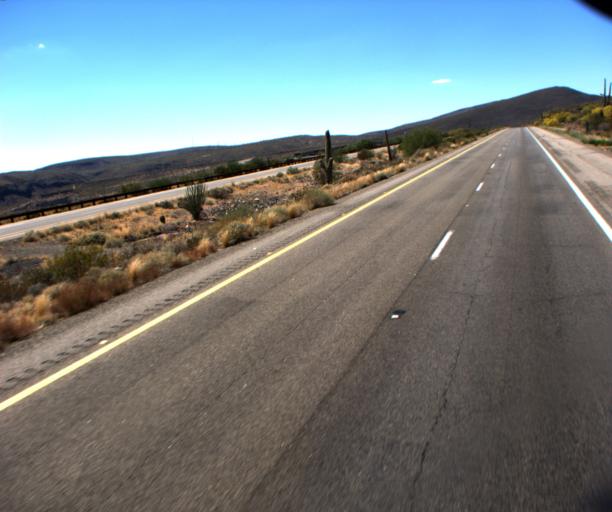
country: US
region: Arizona
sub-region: Yavapai County
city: Bagdad
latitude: 34.5364
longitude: -113.4336
